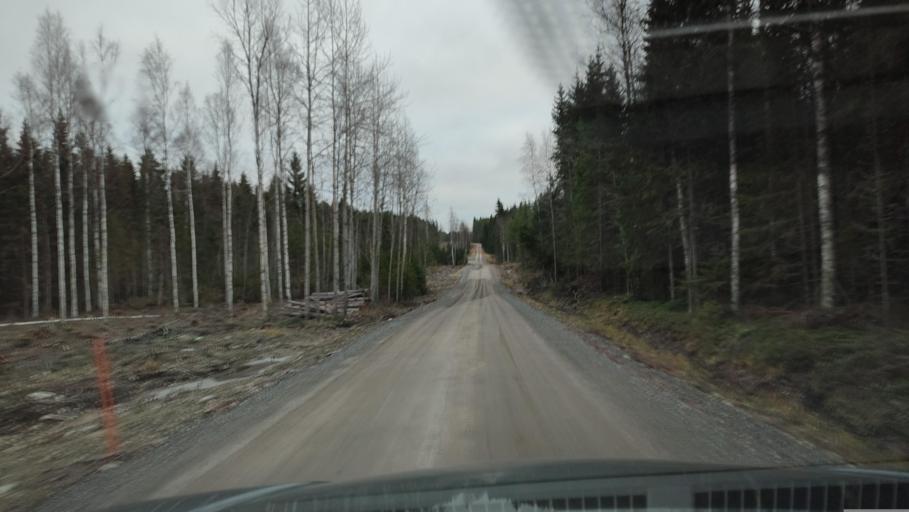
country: FI
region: Southern Ostrobothnia
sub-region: Suupohja
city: Karijoki
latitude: 62.2045
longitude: 21.5943
